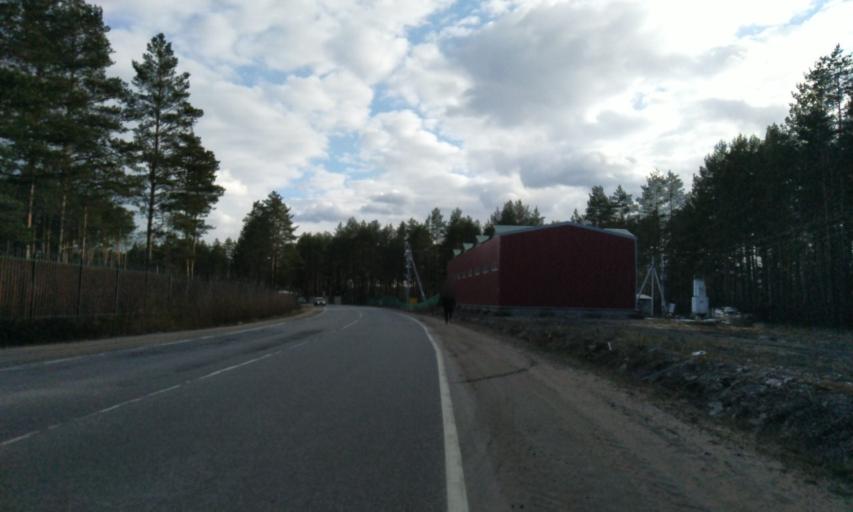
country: RU
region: Leningrad
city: Novoye Devyatkino
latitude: 60.1213
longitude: 30.4492
